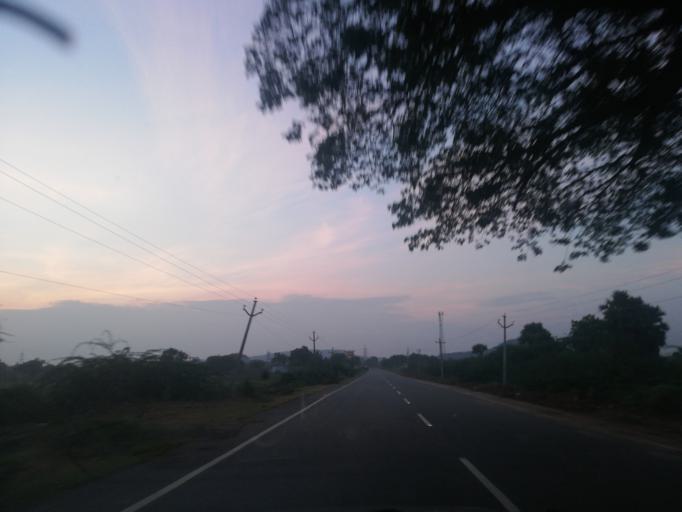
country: IN
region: Andhra Pradesh
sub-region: Guntur
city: Macherla
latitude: 16.6789
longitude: 79.2627
